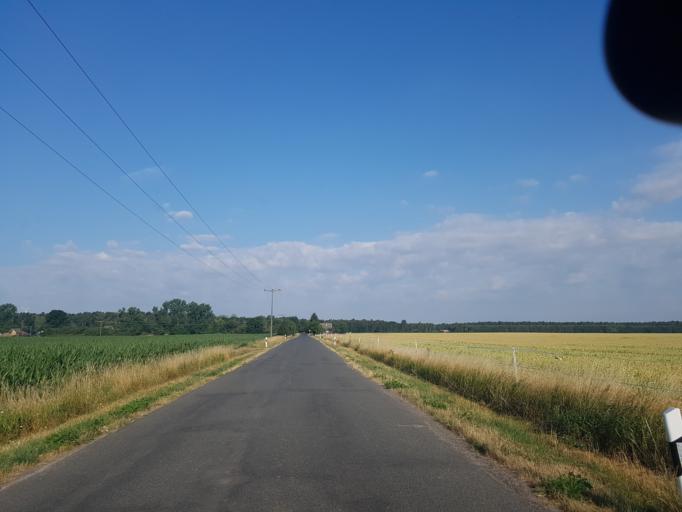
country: DE
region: Saxony-Anhalt
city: Seyda
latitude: 51.9237
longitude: 12.9257
